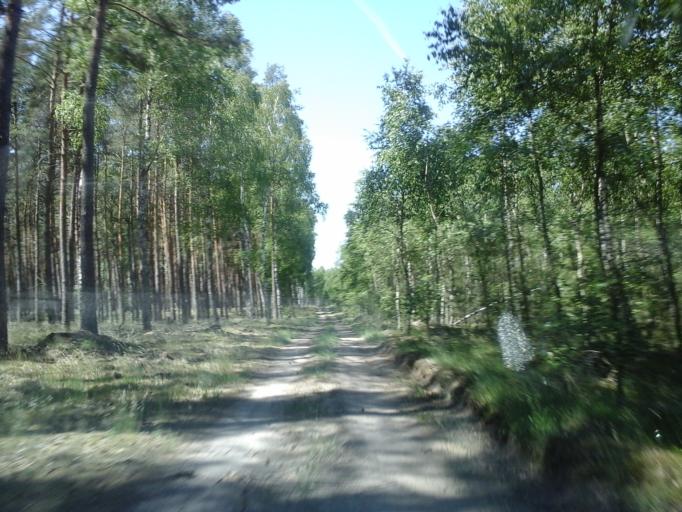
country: PL
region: West Pomeranian Voivodeship
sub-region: Powiat drawski
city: Kalisz Pomorski
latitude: 53.1421
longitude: 15.9034
